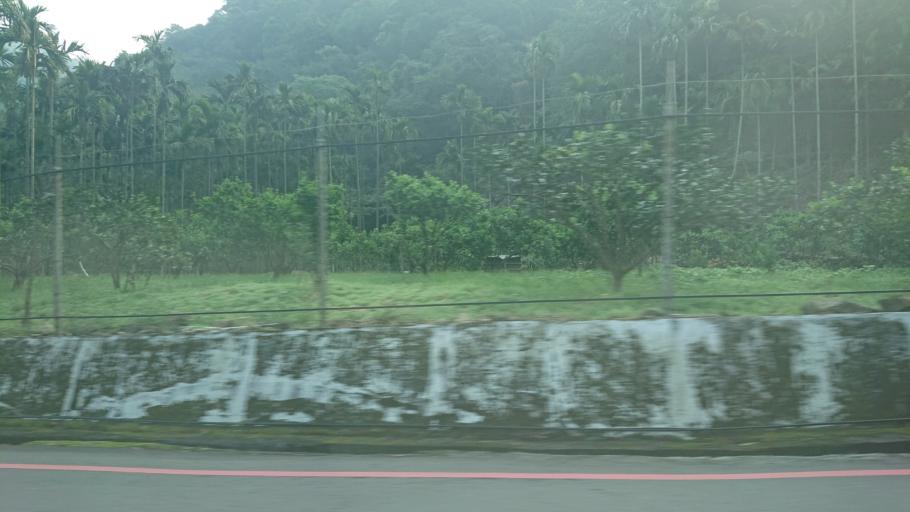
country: TW
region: Taiwan
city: Daxi
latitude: 24.8629
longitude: 121.4216
